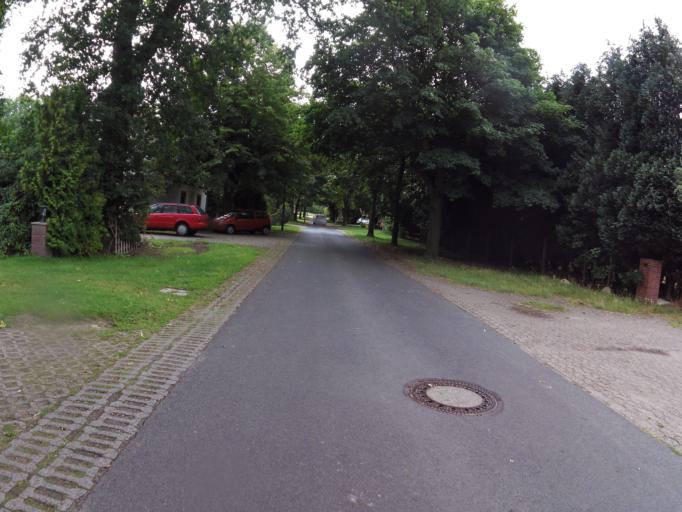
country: DE
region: Lower Saxony
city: Loxstedt
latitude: 53.4972
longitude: 8.7057
